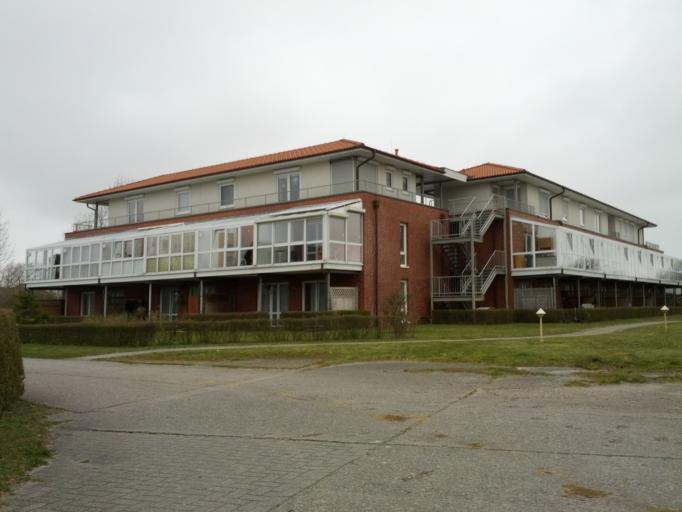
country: DE
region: Lower Saxony
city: Langeoog
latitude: 53.7423
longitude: 7.4793
